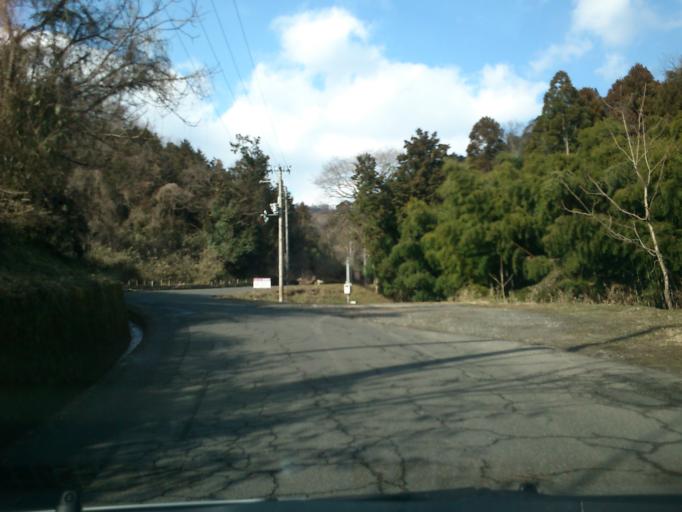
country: JP
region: Kyoto
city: Miyazu
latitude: 35.5815
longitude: 135.1773
